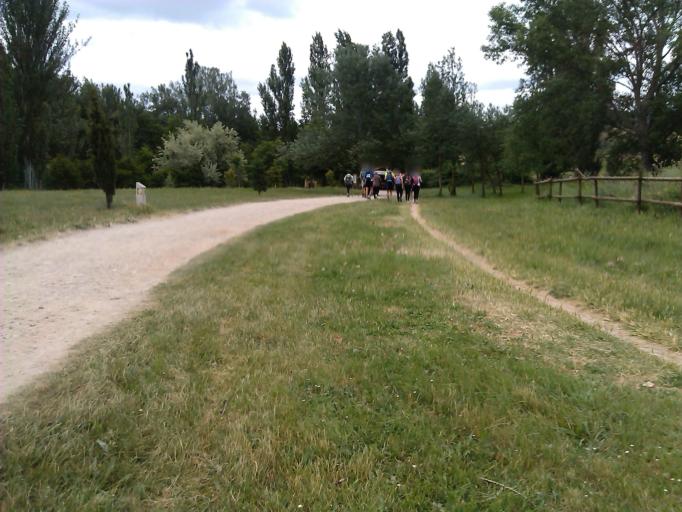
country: ES
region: La Rioja
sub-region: Provincia de La Rioja
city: Navarrete
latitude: 42.4422
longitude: -2.5133
